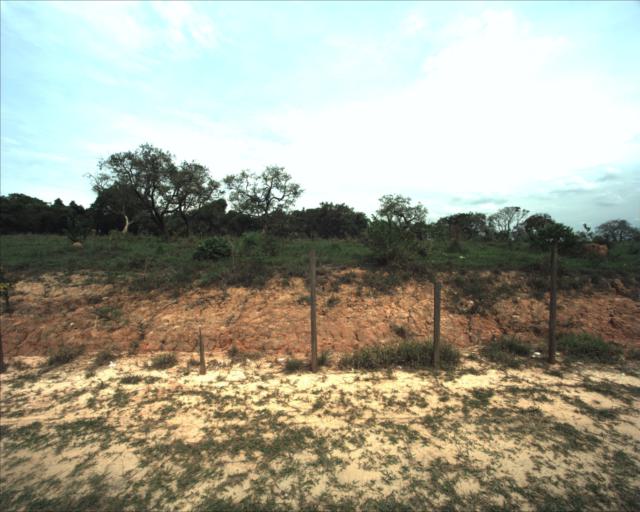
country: BR
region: Sao Paulo
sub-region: Sorocaba
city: Sorocaba
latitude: -23.4275
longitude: -47.4259
